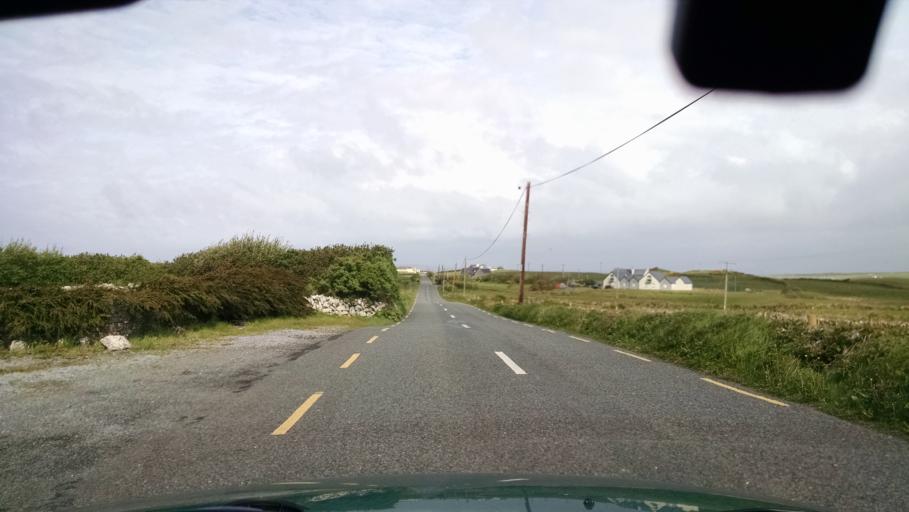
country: IE
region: Connaught
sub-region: County Galway
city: Bearna
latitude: 53.0102
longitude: -9.3628
